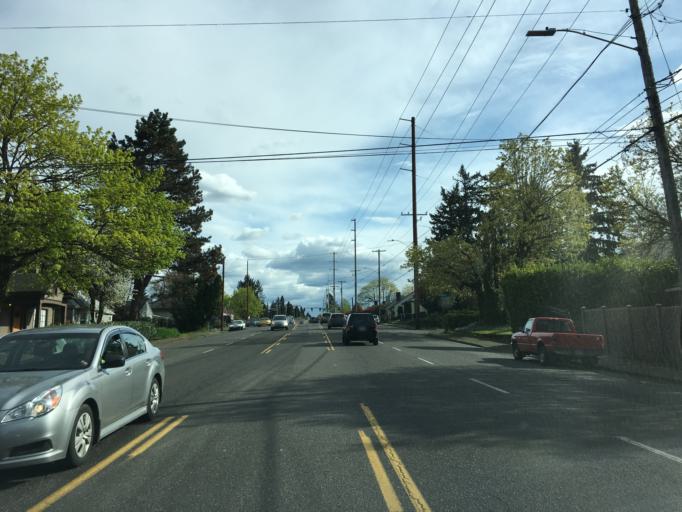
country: US
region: Oregon
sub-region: Multnomah County
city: Lents
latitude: 45.5500
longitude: -122.5578
